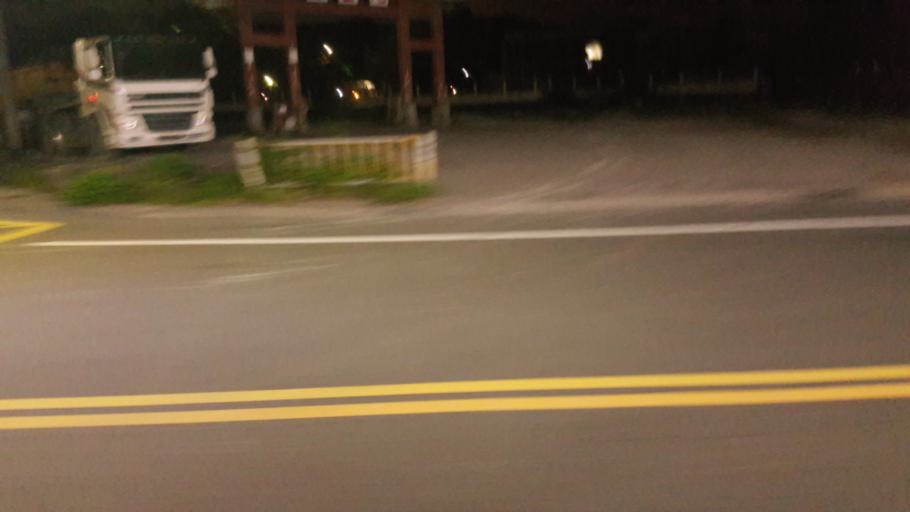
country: TW
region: Taiwan
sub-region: Hsinchu
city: Hsinchu
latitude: 24.7690
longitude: 120.9773
